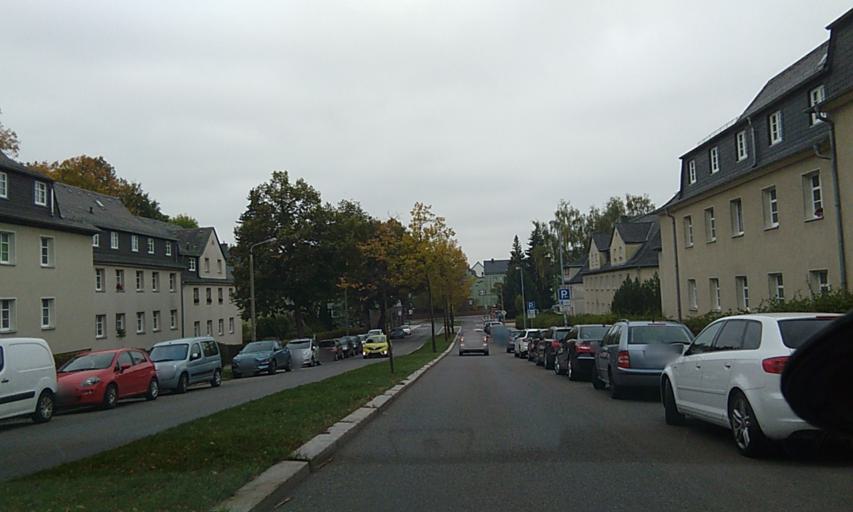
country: DE
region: Saxony
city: Chemnitz
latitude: 50.8408
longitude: 12.8872
